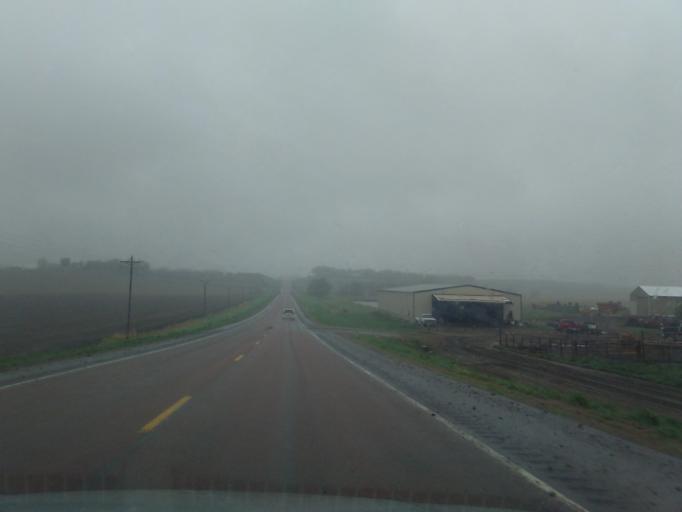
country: US
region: Nebraska
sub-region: Wayne County
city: Wayne
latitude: 42.2354
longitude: -97.1645
